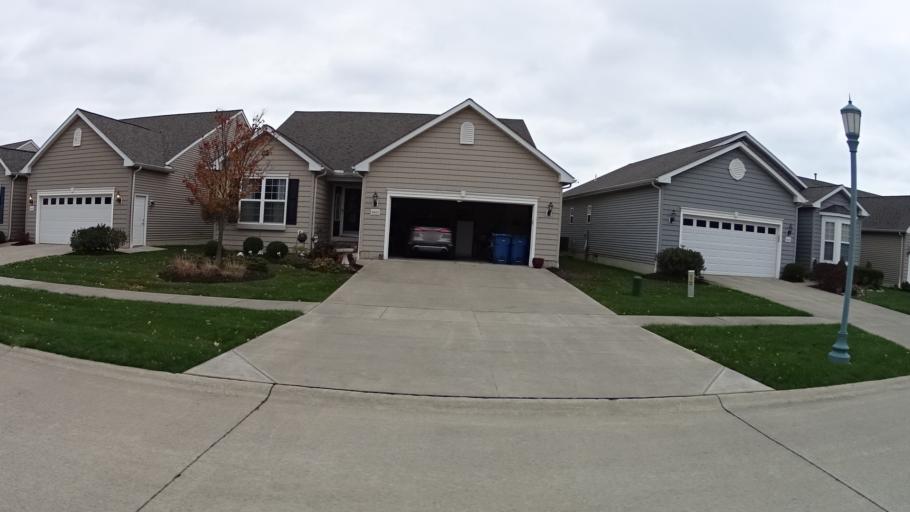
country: US
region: Ohio
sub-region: Lorain County
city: Amherst
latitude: 41.4366
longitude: -82.2288
